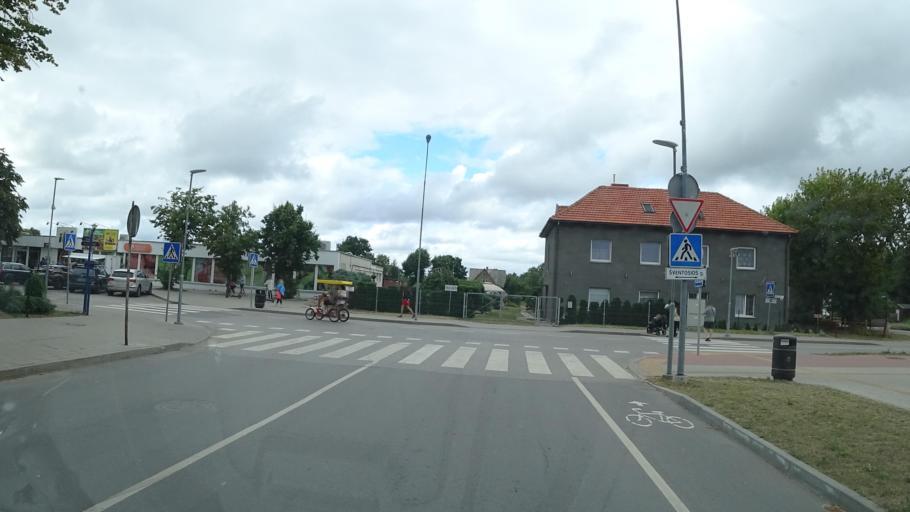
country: LT
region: Klaipedos apskritis
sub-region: Palanga
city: Sventoji
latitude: 56.0308
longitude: 21.0866
